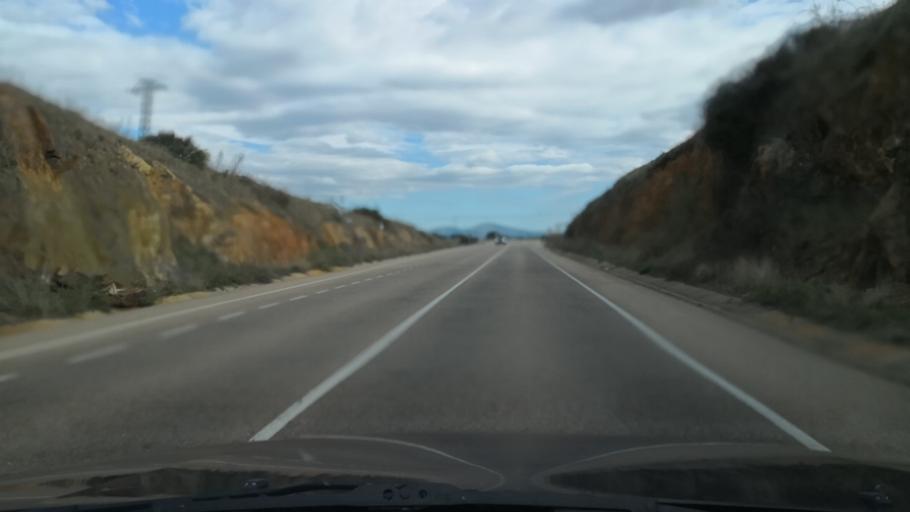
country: ES
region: Castille and Leon
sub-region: Provincia de Salamanca
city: Herguijuela de Ciudad Rodrigo
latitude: 40.4835
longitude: -6.5807
